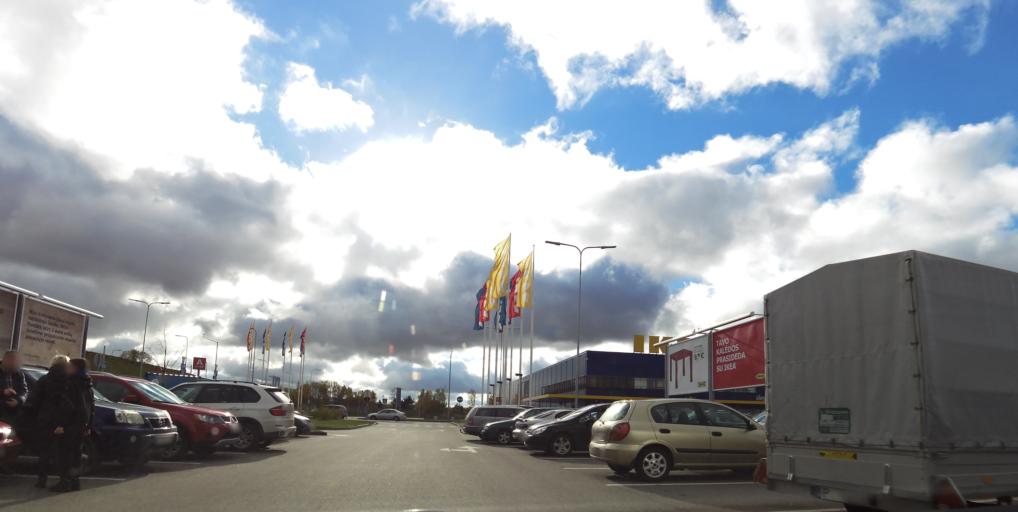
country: LT
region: Vilnius County
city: Naujamiestis
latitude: 54.6522
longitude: 25.2817
